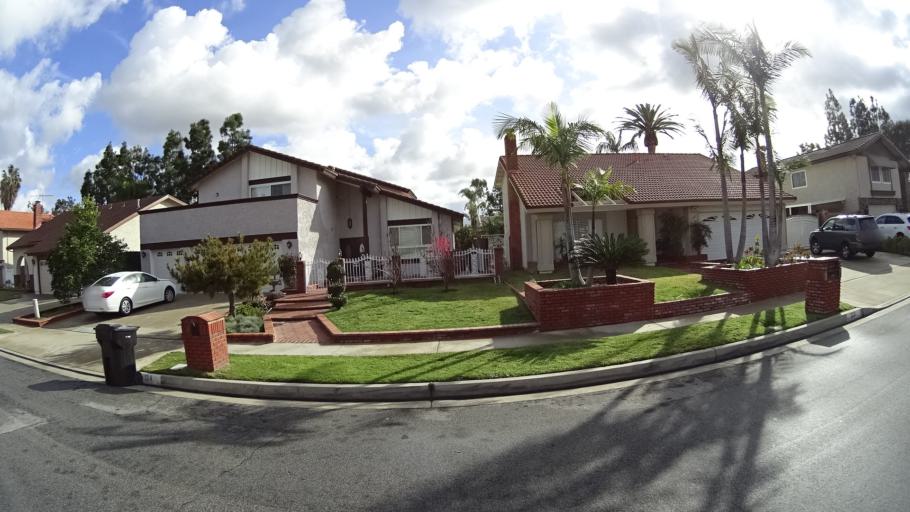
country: US
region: California
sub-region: Orange County
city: Villa Park
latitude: 33.8512
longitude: -117.7854
